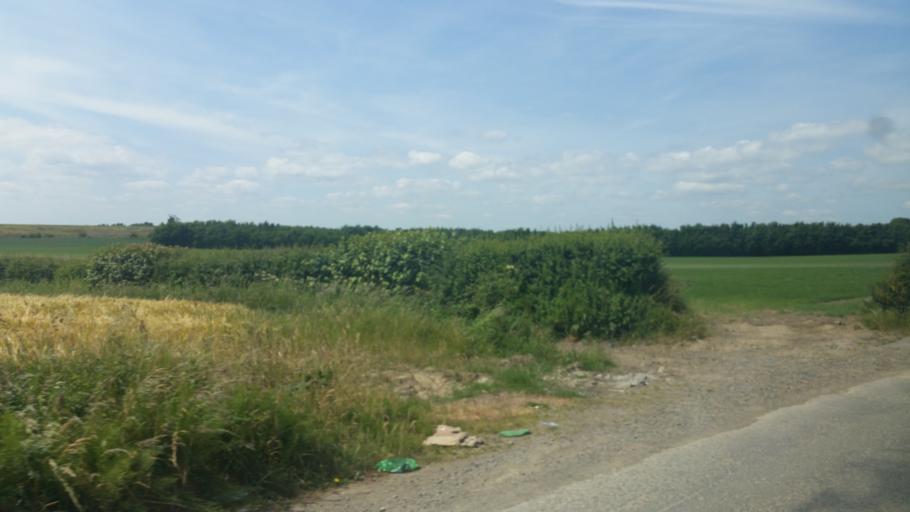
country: IE
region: Leinster
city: Lusk
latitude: 53.5349
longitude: -6.1797
